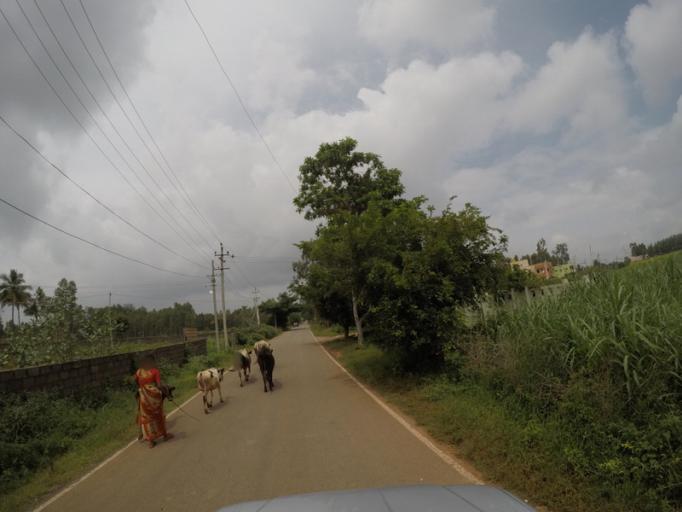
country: IN
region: Karnataka
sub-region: Bangalore Urban
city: Yelahanka
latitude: 13.1366
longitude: 77.5111
